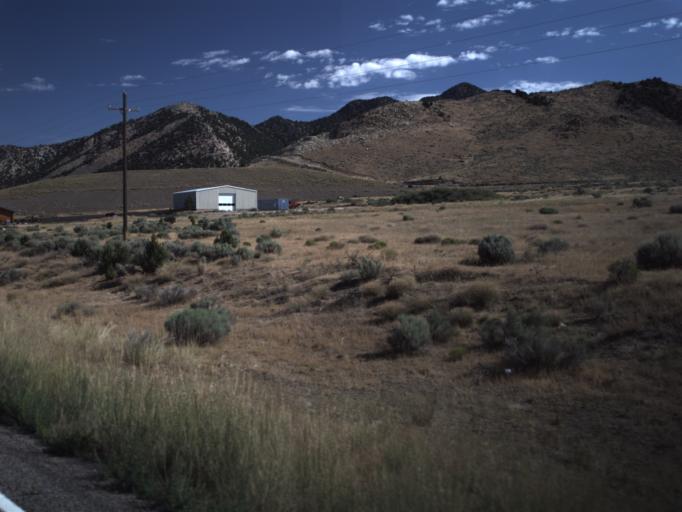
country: US
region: Utah
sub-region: Juab County
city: Mona
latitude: 39.9090
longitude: -112.1405
